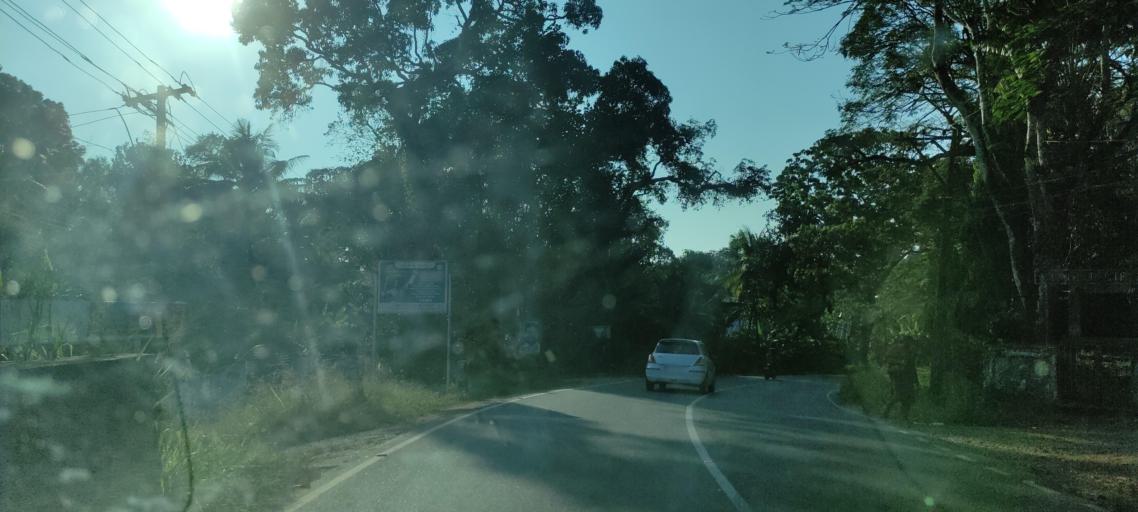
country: IN
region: Kerala
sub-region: Pattanamtitta
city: Adur
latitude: 9.1649
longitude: 76.6882
